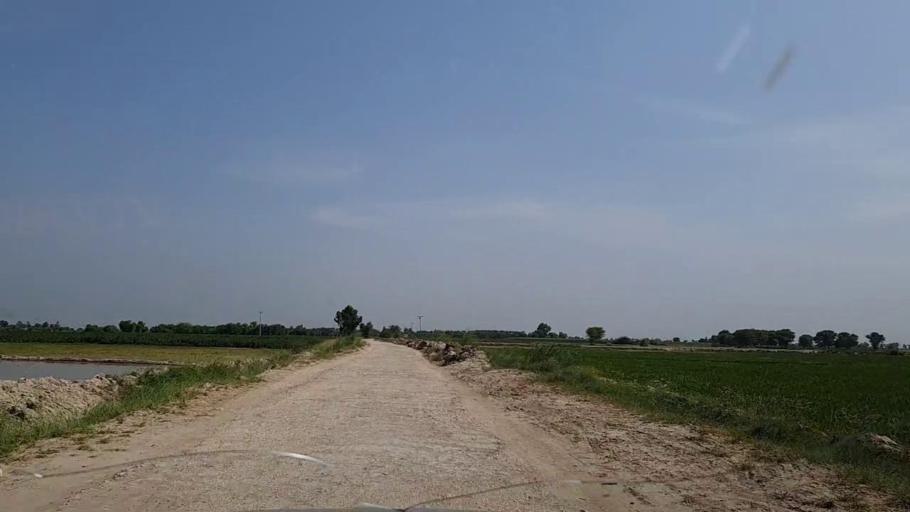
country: PK
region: Sindh
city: Khanpur
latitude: 27.7920
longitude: 69.3168
